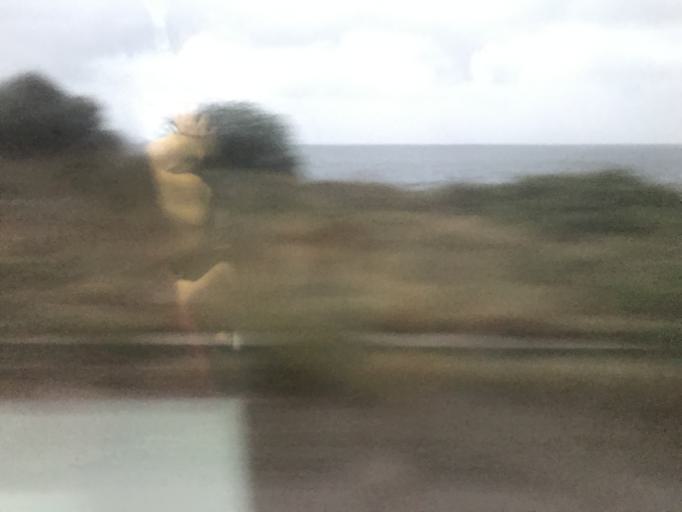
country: TR
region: Kocaeli
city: Tavsancil
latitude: 40.7717
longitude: 29.5848
